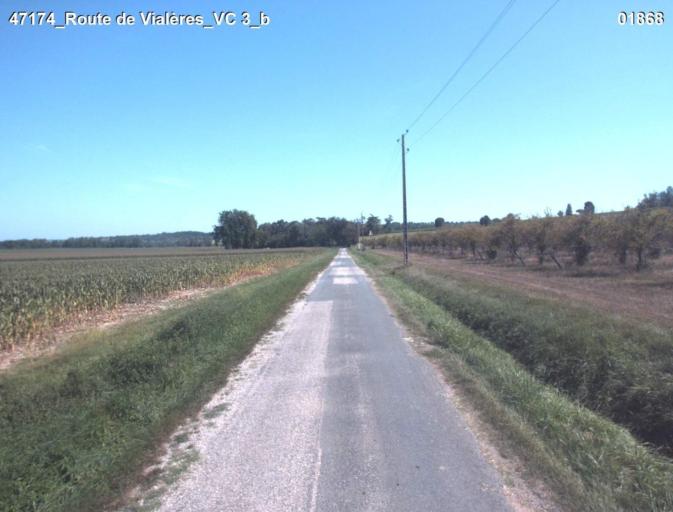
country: FR
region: Aquitaine
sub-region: Departement du Lot-et-Garonne
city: Nerac
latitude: 44.0498
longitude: 0.3815
